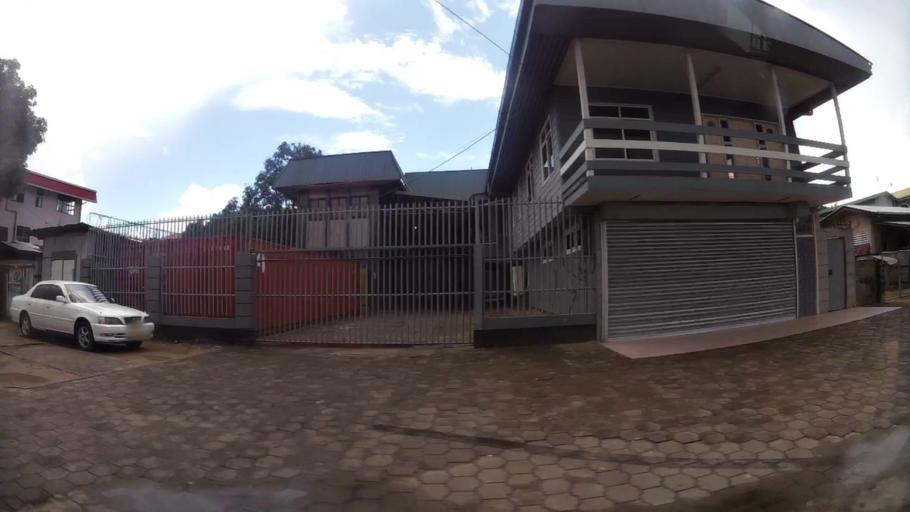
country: SR
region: Paramaribo
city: Paramaribo
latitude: 5.8328
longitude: -55.1677
